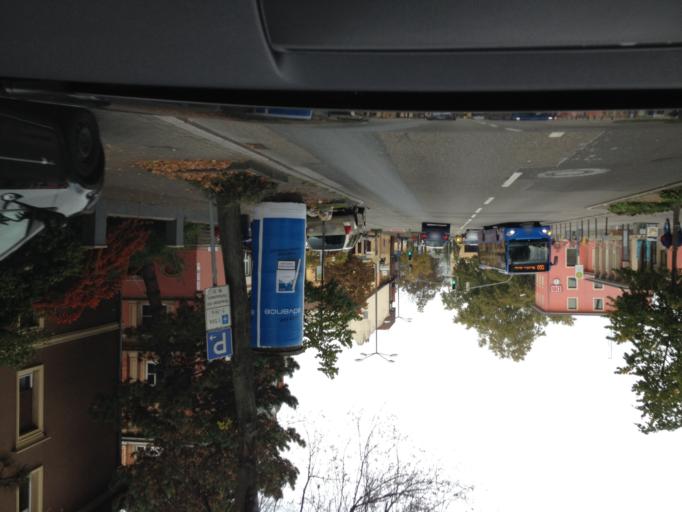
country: DE
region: Rheinland-Pfalz
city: Speyer
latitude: 49.3235
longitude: 8.4288
